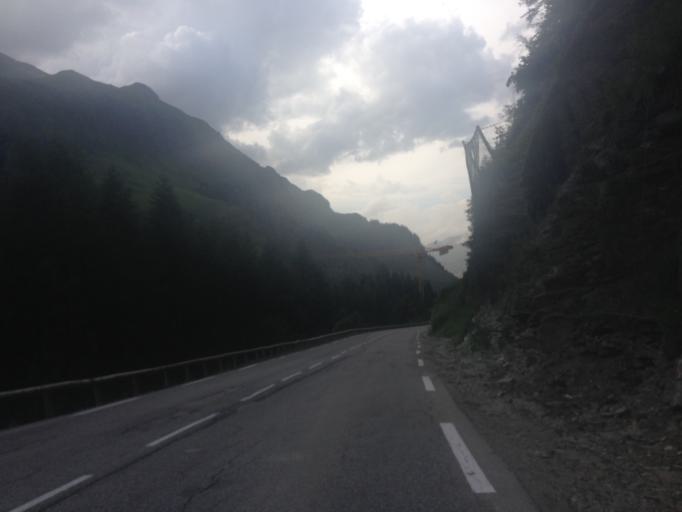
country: FR
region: Rhone-Alpes
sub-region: Departement de la Savoie
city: Tignes
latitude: 45.5141
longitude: 6.9173
